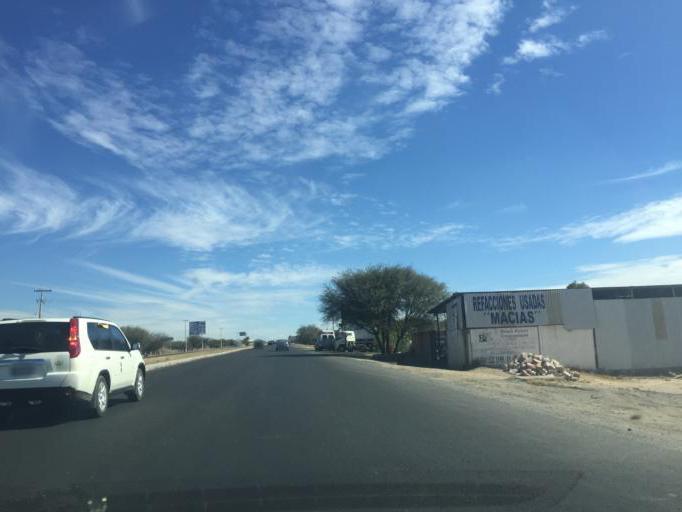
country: MX
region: Queretaro
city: San Nicolas
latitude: 20.5003
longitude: -99.9254
